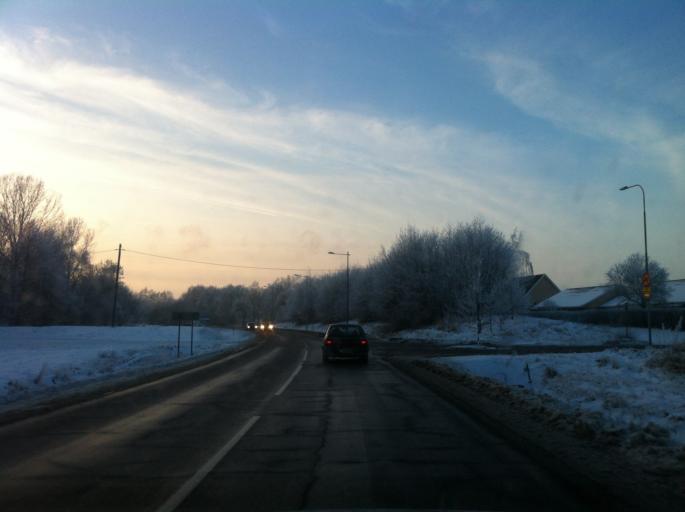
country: SE
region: Skane
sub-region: Bjuvs Kommun
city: Billesholm
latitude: 56.0267
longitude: 13.0432
